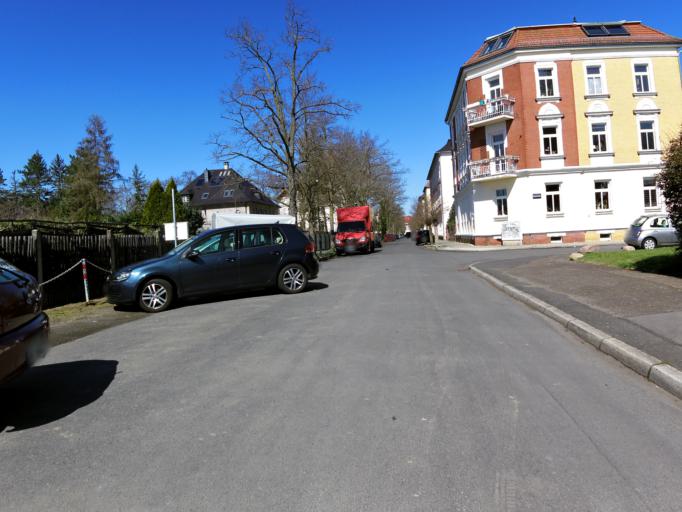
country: DE
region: Saxony
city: Markkleeberg
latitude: 51.2756
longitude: 12.3753
